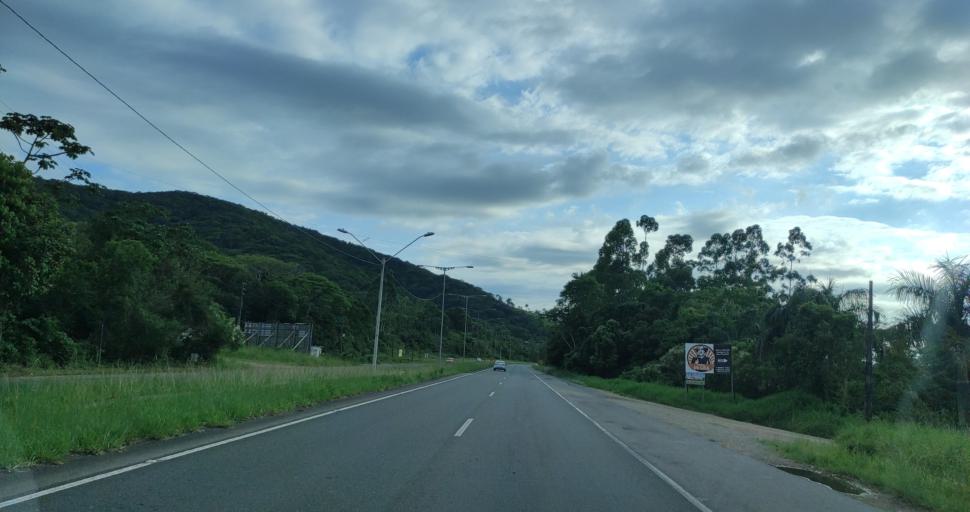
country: BR
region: Santa Catarina
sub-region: Penha
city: Penha
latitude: -26.8115
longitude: -48.6587
